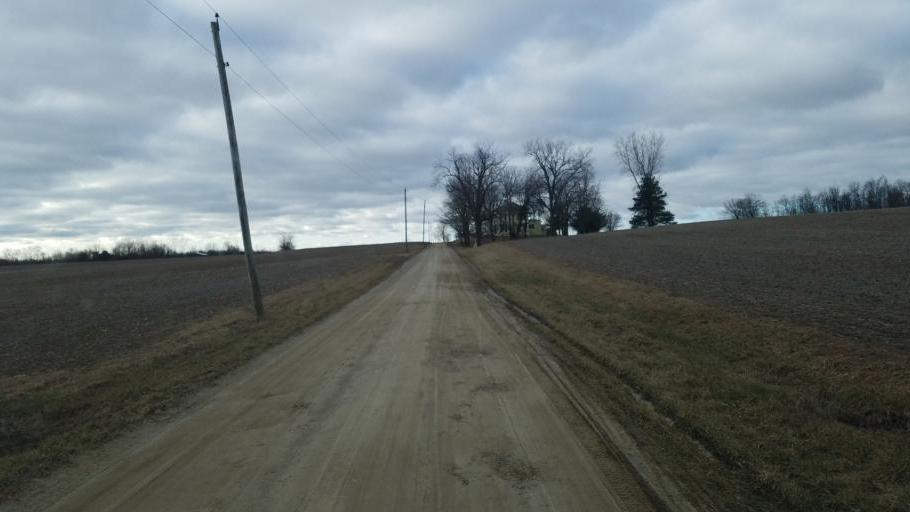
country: US
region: Ohio
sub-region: Richland County
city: Lexington
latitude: 40.5838
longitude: -82.6757
